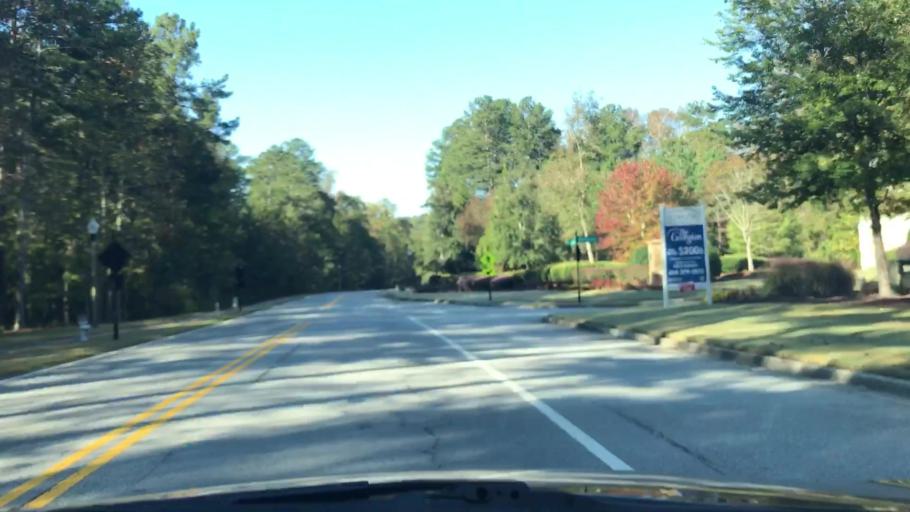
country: US
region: Georgia
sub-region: Carroll County
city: Villa Rica
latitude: 33.7991
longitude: -84.9089
